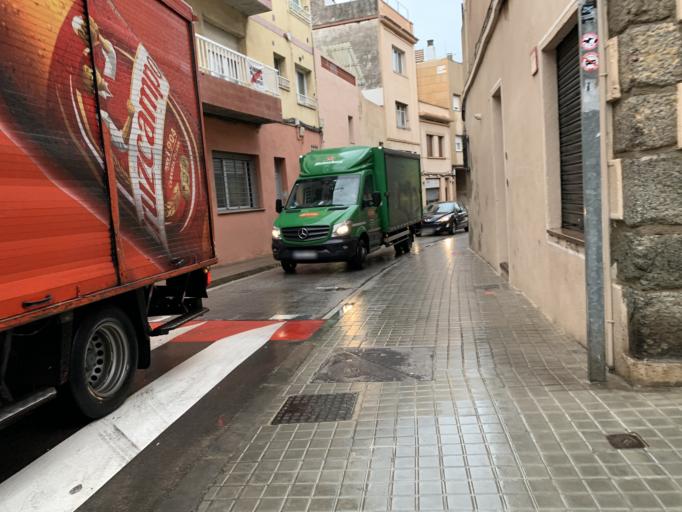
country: ES
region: Catalonia
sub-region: Provincia de Barcelona
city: Mataro
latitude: 41.5408
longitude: 2.4485
